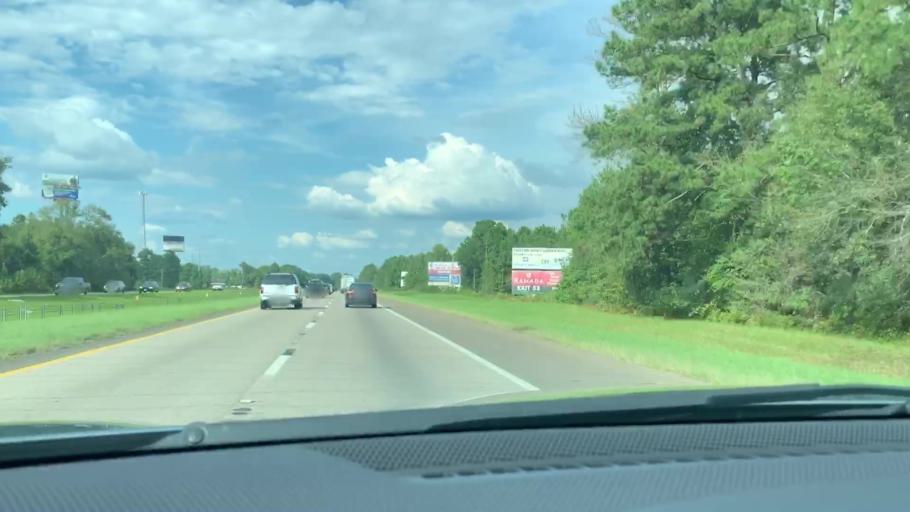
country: US
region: South Carolina
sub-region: Hampton County
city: Yemassee
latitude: 32.6793
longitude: -80.8820
